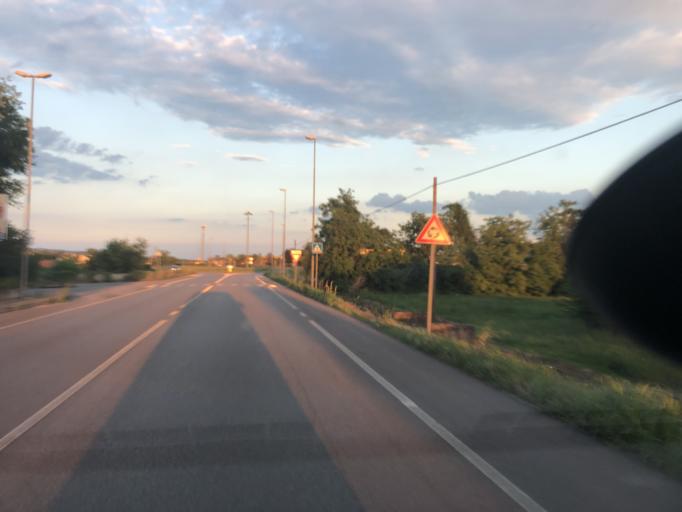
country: IT
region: Veneto
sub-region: Provincia di Verona
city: Pescantina
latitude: 45.4930
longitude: 10.8795
